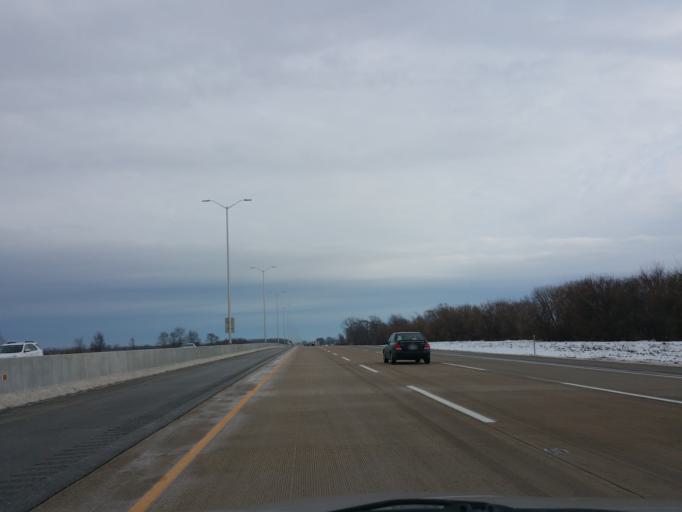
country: US
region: Illinois
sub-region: McHenry County
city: Marengo
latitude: 42.2062
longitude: -88.7040
